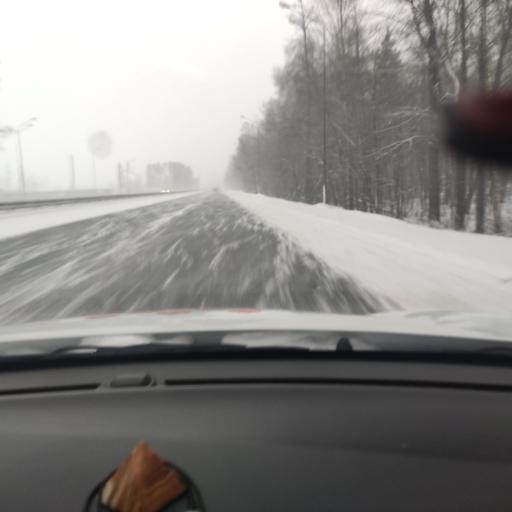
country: RU
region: Tatarstan
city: Osinovo
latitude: 55.8458
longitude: 48.8526
